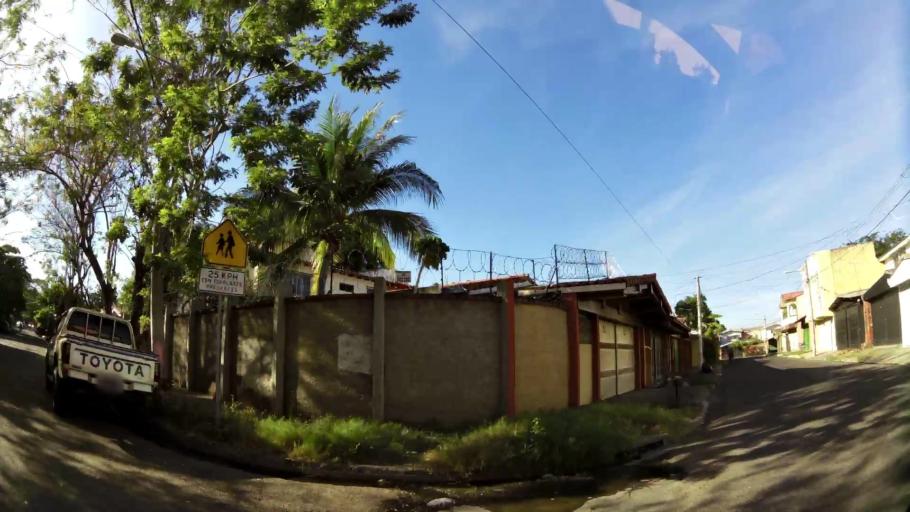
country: SV
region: San Miguel
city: San Miguel
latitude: 13.4731
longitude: -88.1857
